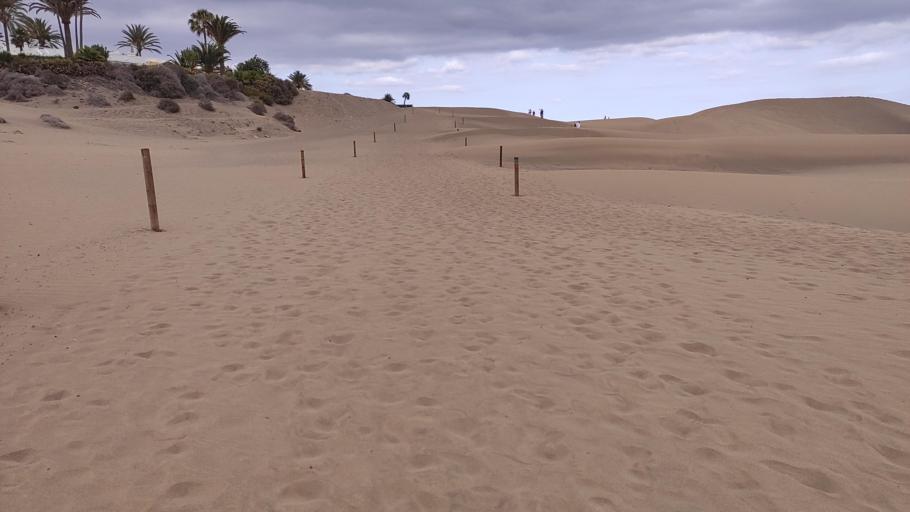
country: ES
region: Canary Islands
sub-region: Provincia de Las Palmas
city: Playa del Ingles
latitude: 27.7450
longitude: -15.5783
